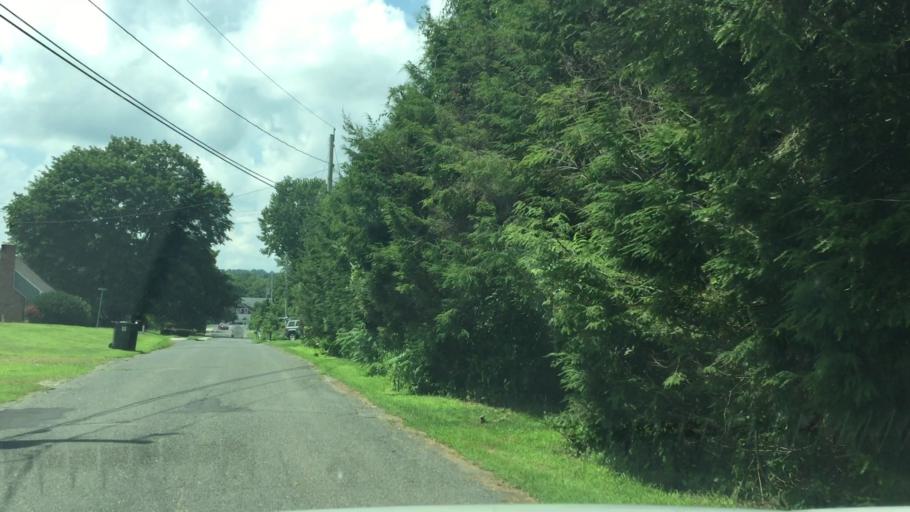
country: US
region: Massachusetts
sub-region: Berkshire County
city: Great Barrington
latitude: 42.2075
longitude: -73.3432
